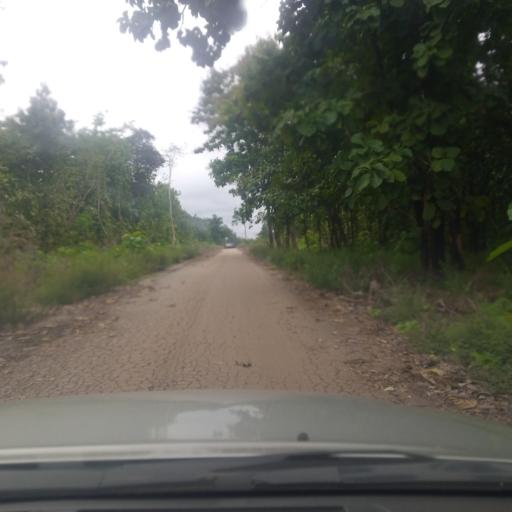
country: NG
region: Ebonyi
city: Effium
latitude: 6.6231
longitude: 8.0470
